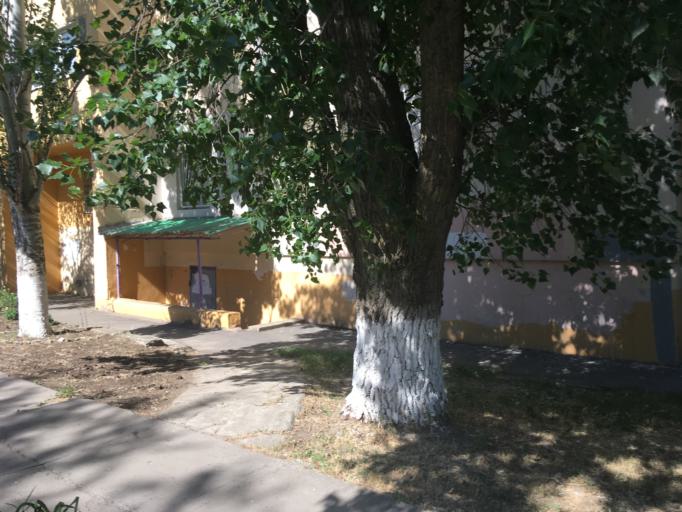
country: RU
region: Rostov
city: Rostov-na-Donu
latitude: 47.2091
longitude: 39.6267
